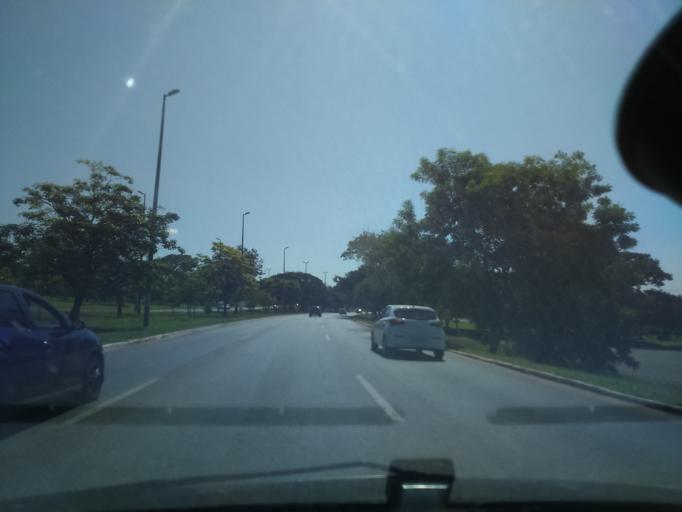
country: BR
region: Federal District
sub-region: Brasilia
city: Brasilia
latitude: -15.8255
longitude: -47.8874
